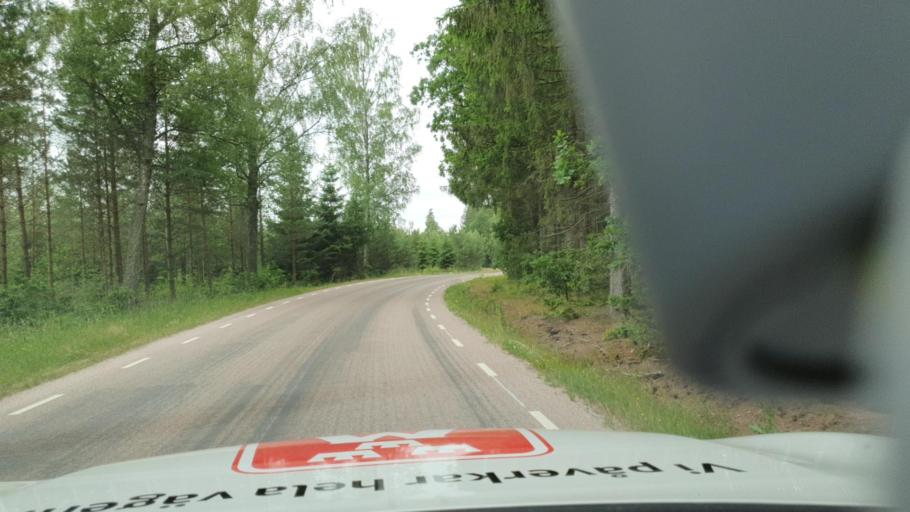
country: SE
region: Vaestra Goetaland
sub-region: Skara Kommun
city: Skara
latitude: 58.4677
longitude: 13.4229
